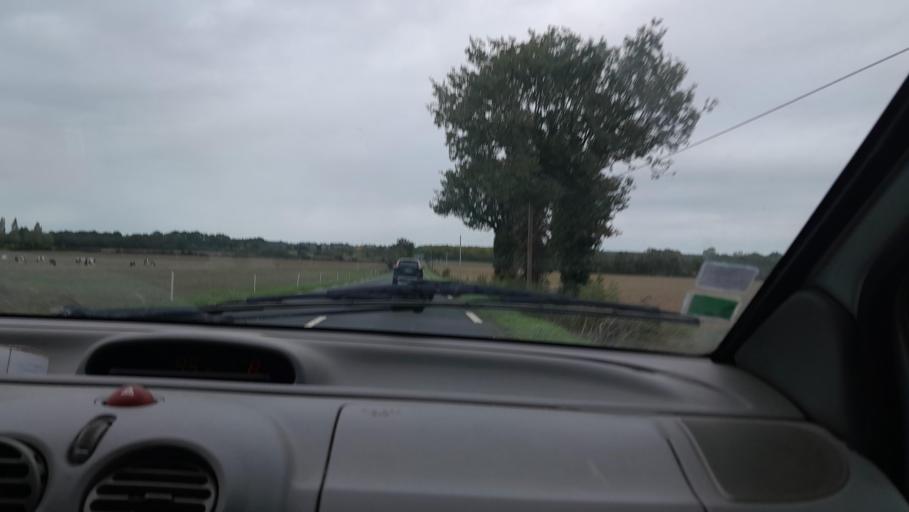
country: FR
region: Pays de la Loire
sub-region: Departement de la Loire-Atlantique
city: Saint-Mars-la-Jaille
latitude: 47.4750
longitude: -1.1746
